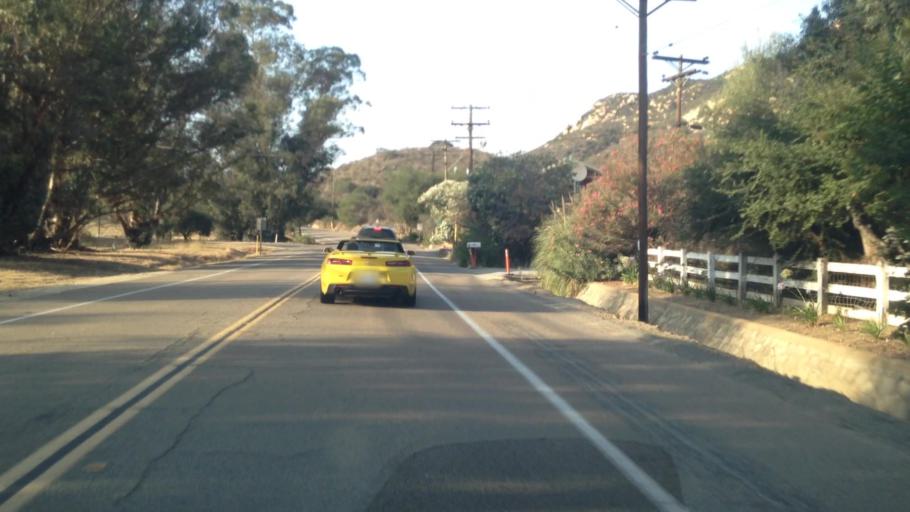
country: US
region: California
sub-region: San Diego County
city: Rainbow
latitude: 33.4272
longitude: -117.1419
